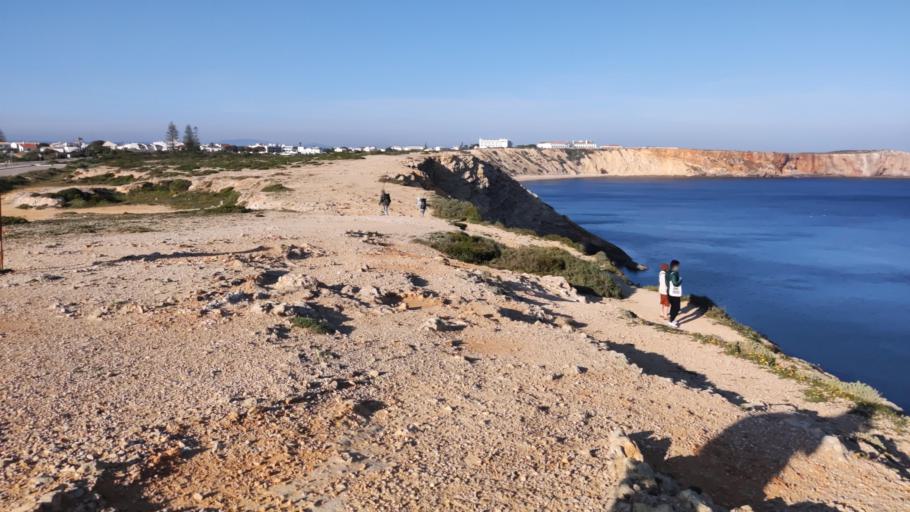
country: PT
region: Faro
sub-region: Vila do Bispo
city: Sagres
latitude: 37.0023
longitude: -8.9460
